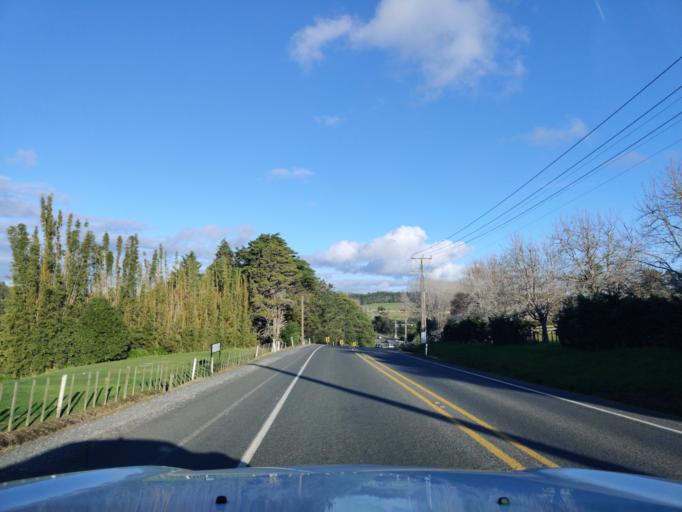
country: NZ
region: Auckland
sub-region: Auckland
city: Pakuranga
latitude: -36.9532
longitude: 174.9680
